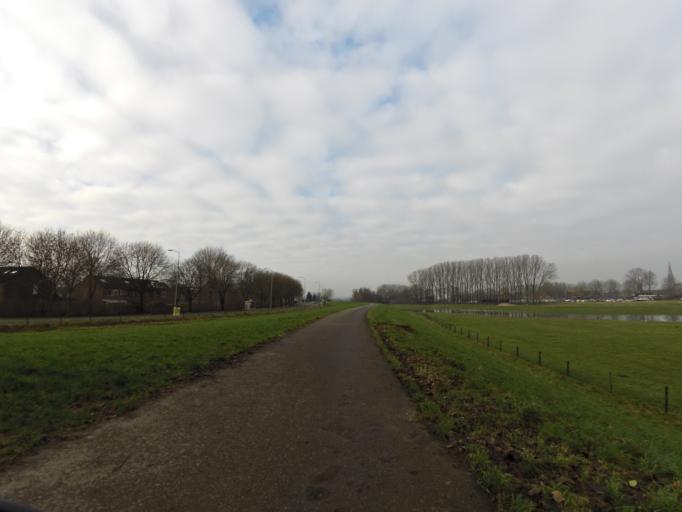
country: NL
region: Gelderland
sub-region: Gemeente Doesburg
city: Doesburg
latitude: 52.0046
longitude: 6.1347
